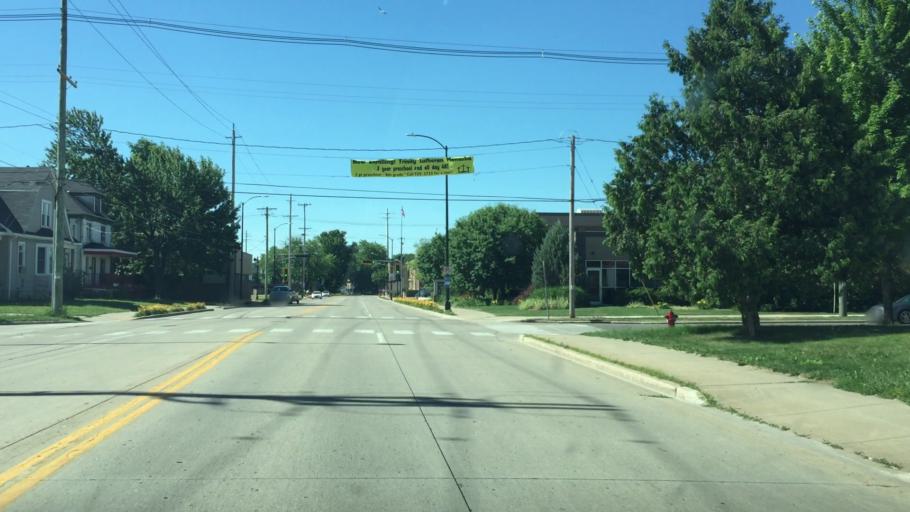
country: US
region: Wisconsin
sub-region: Winnebago County
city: Menasha
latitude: 44.2042
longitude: -88.4462
